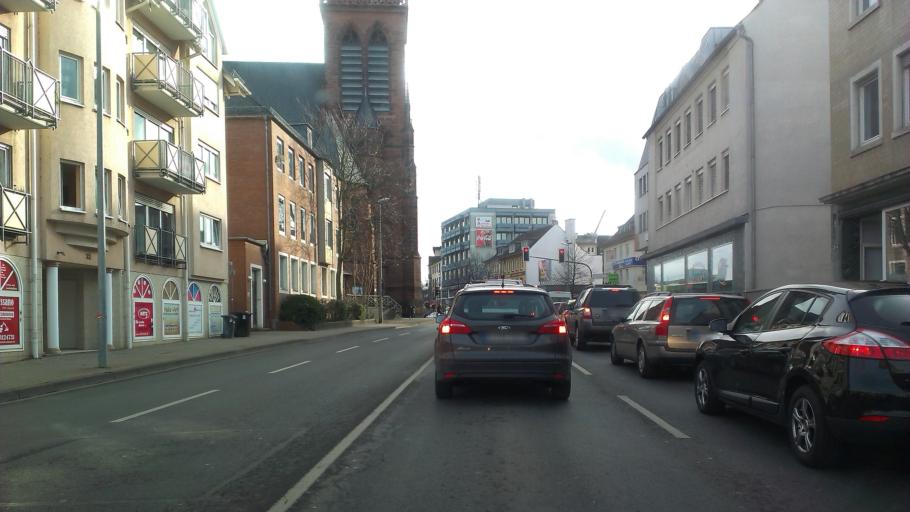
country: DE
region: Rheinland-Pfalz
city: Bad Kreuznach
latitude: 49.8436
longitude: 7.8629
